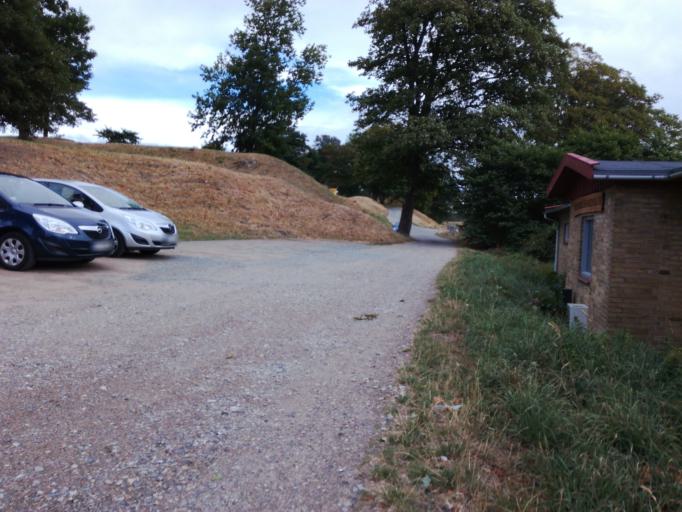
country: DK
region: South Denmark
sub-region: Fredericia Kommune
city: Fredericia
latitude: 55.5605
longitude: 9.7684
